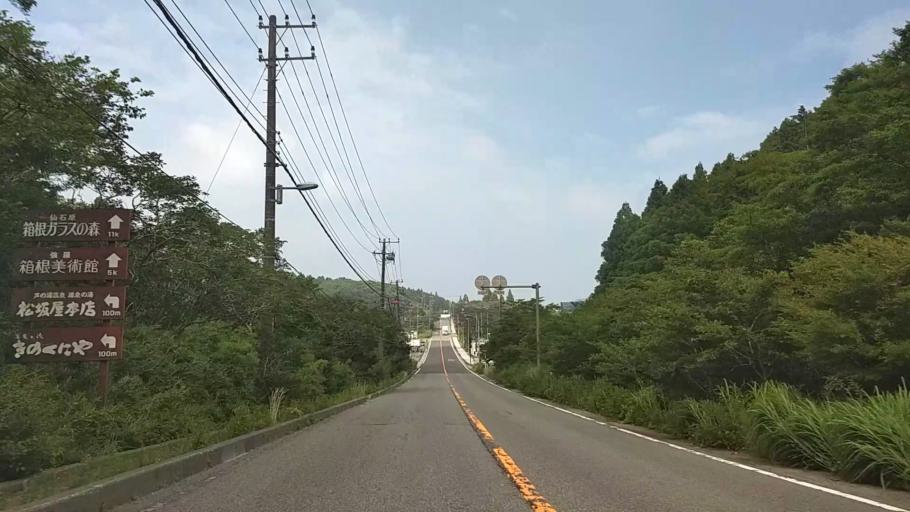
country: JP
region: Kanagawa
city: Hakone
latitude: 35.2188
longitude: 139.0405
